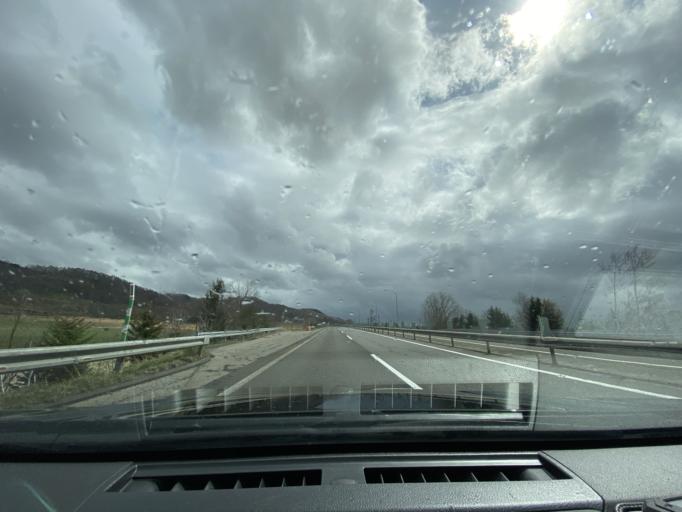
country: JP
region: Hokkaido
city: Sunagawa
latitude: 43.4399
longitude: 141.9163
